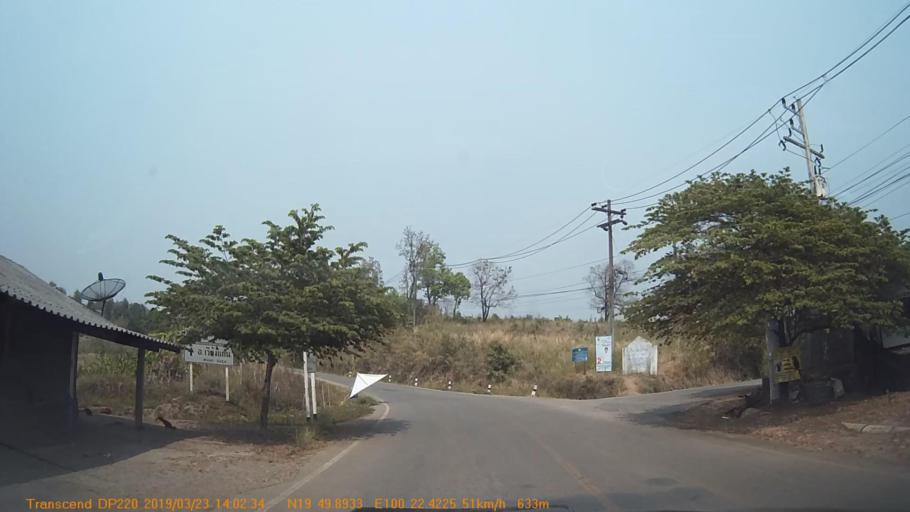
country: TH
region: Chiang Rai
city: Khun Tan
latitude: 19.8316
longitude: 100.3737
